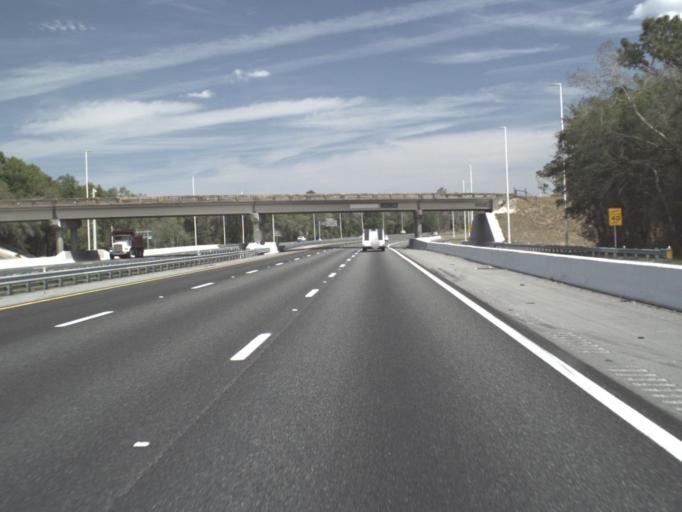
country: US
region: Florida
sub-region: Hernando County
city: Ridge Manor
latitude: 28.6012
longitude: -82.2034
